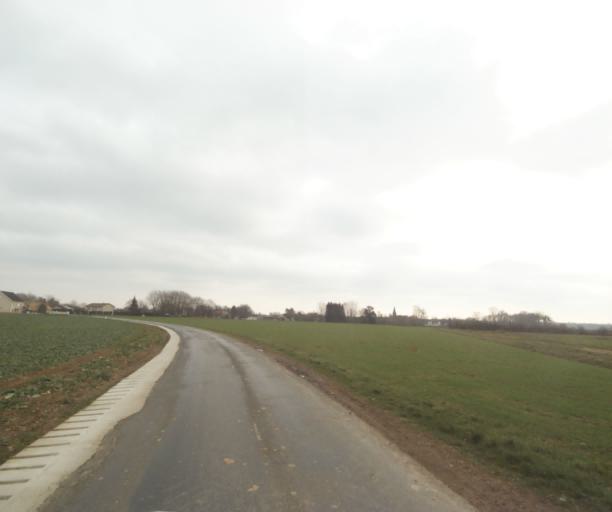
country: FR
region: Champagne-Ardenne
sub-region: Departement de la Haute-Marne
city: Villiers-en-Lieu
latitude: 48.6831
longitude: 4.8281
